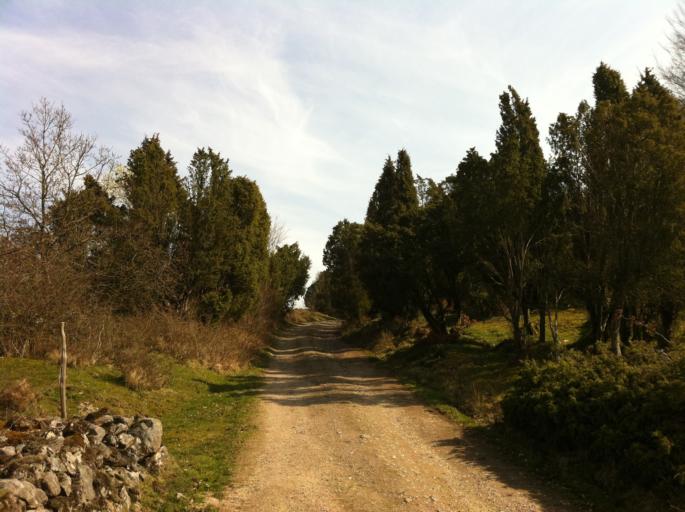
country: SE
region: Skane
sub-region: Eslovs Kommun
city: Stehag
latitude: 56.0108
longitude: 13.3716
